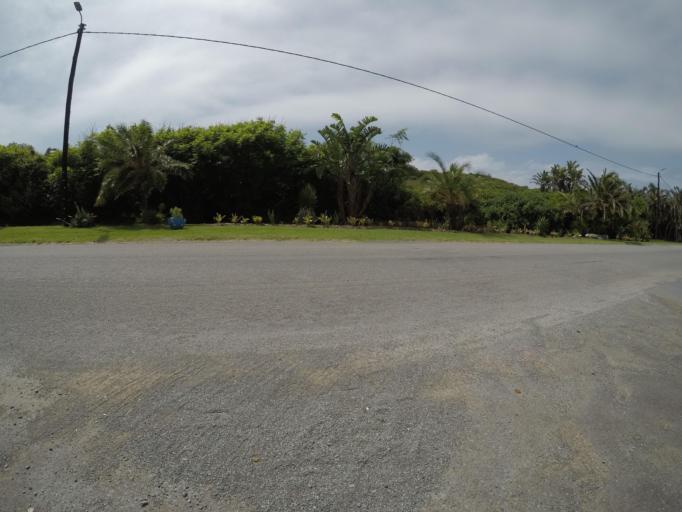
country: ZA
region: Eastern Cape
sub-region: Buffalo City Metropolitan Municipality
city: East London
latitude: -32.9365
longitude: 28.0281
